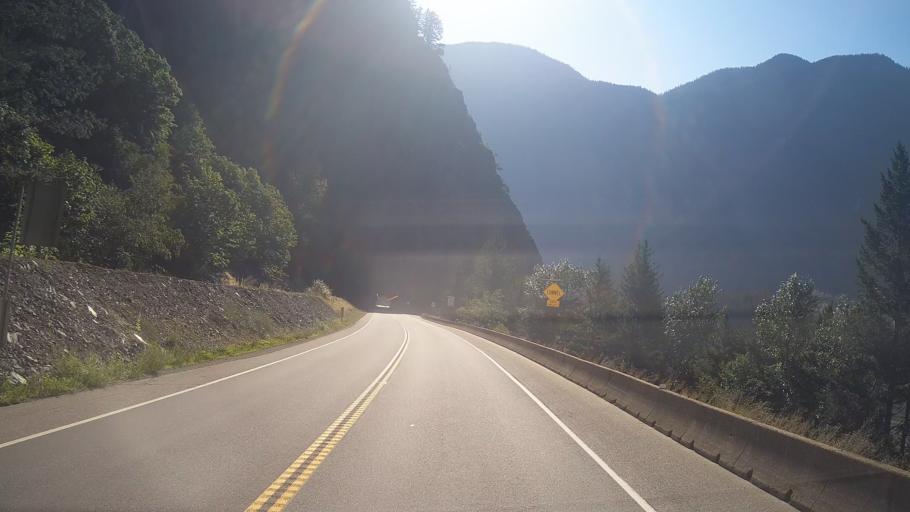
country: CA
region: British Columbia
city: Hope
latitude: 49.5631
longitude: -121.4181
